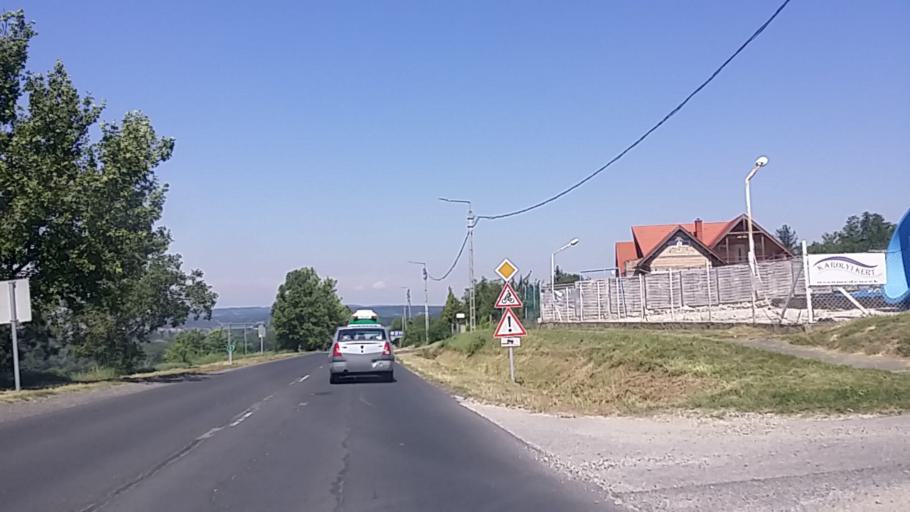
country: HU
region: Zala
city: Cserszegtomaj
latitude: 46.7826
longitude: 17.2196
